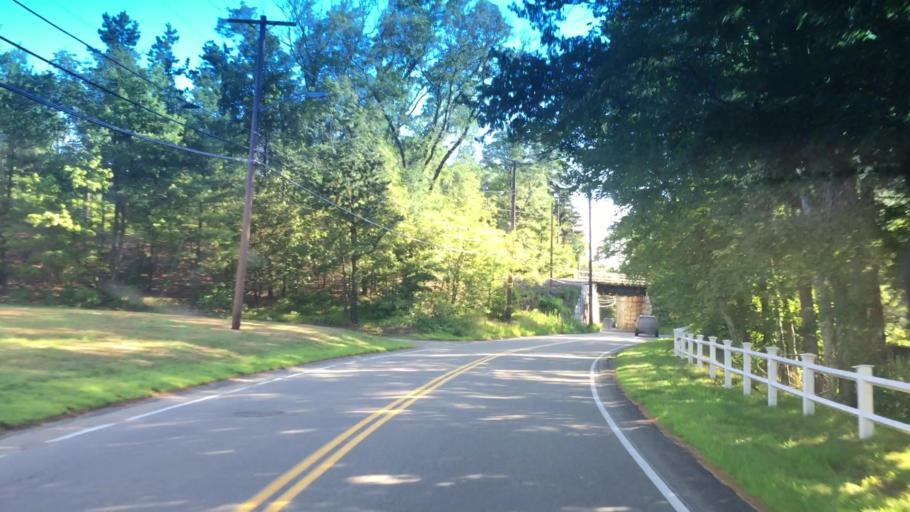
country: US
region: Massachusetts
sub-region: Norfolk County
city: Walpole
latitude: 42.1397
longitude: -71.2711
